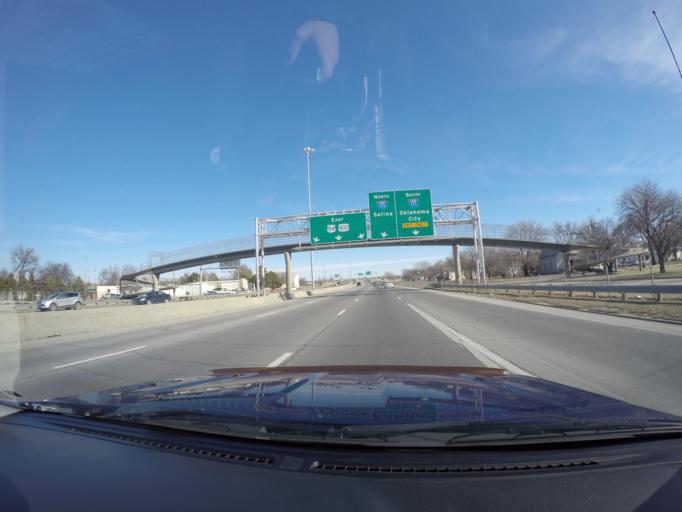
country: US
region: Kansas
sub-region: Sedgwick County
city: Wichita
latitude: 37.6786
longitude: -97.3229
